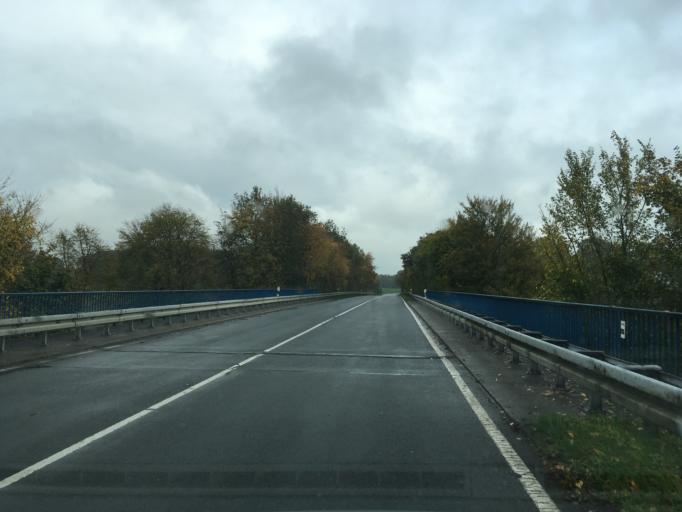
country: DE
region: North Rhine-Westphalia
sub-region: Regierungsbezirk Munster
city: Velen
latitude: 51.8749
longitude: 7.0101
